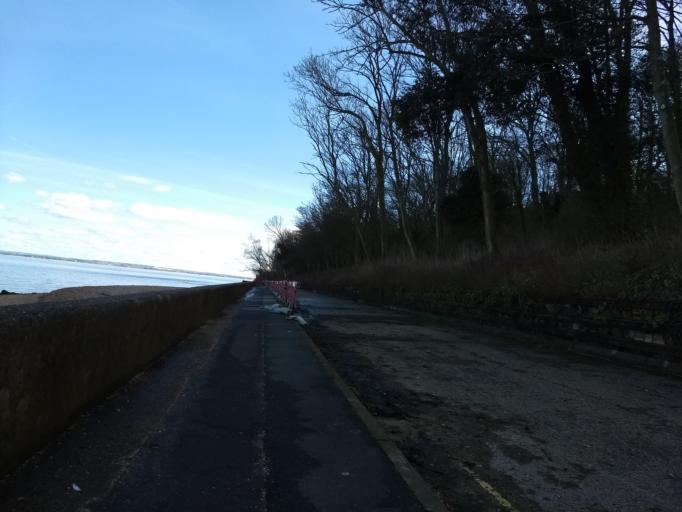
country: GB
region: England
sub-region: Isle of Wight
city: East Cowes
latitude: 50.7650
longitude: -1.2816
